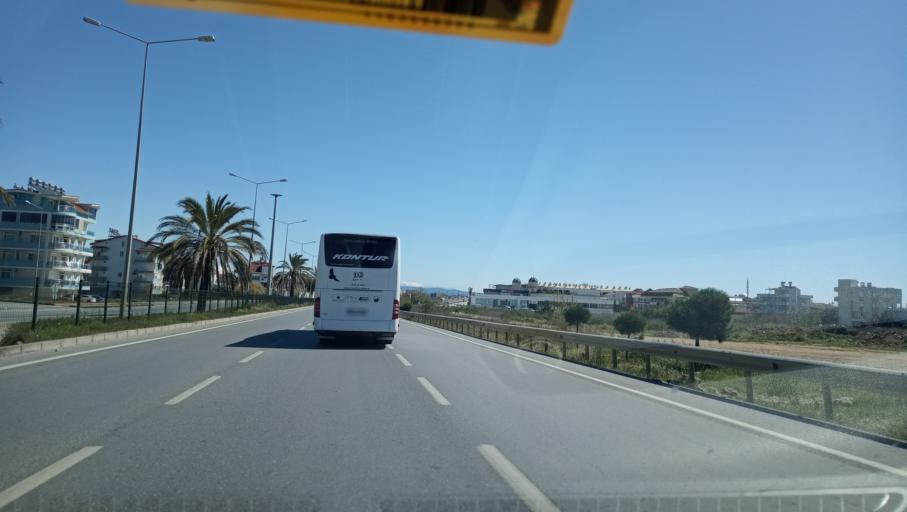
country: TR
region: Antalya
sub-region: Manavgat
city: Manavgat
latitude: 36.7832
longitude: 31.4198
